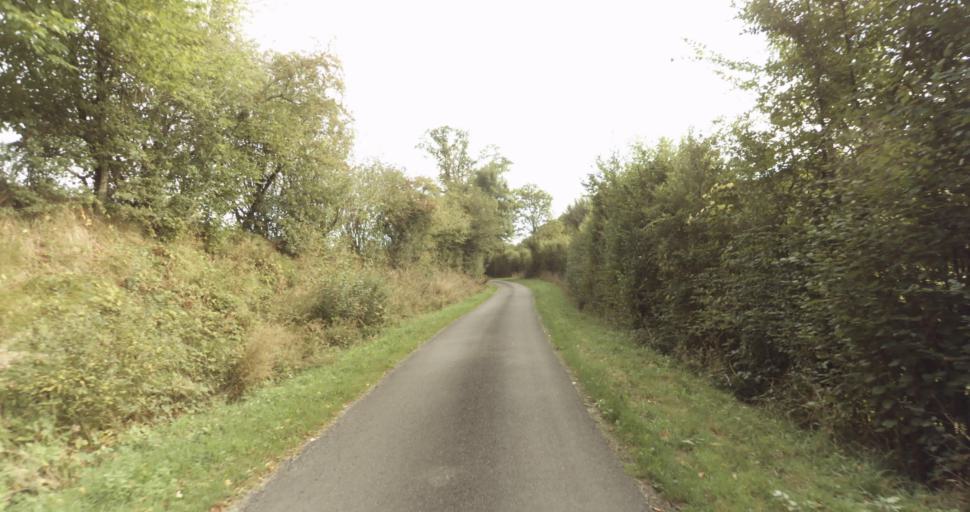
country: FR
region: Lower Normandy
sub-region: Departement de l'Orne
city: Gace
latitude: 48.8314
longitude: 0.2214
